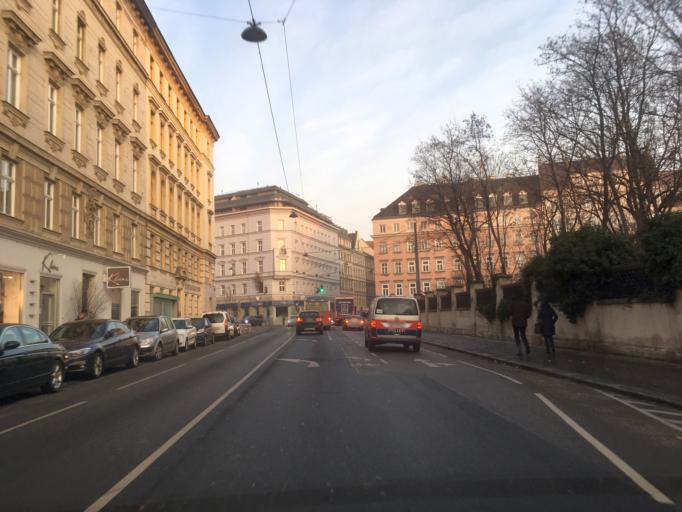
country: AT
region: Vienna
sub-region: Wien Stadt
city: Vienna
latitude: 48.2242
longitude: 16.3574
